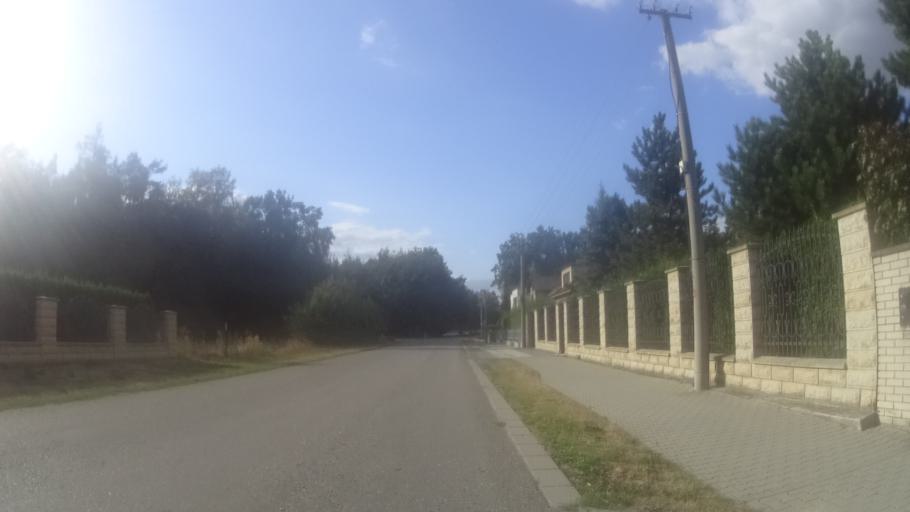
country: CZ
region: Kralovehradecky
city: Trebechovice pod Orebem
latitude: 50.1930
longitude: 16.0033
